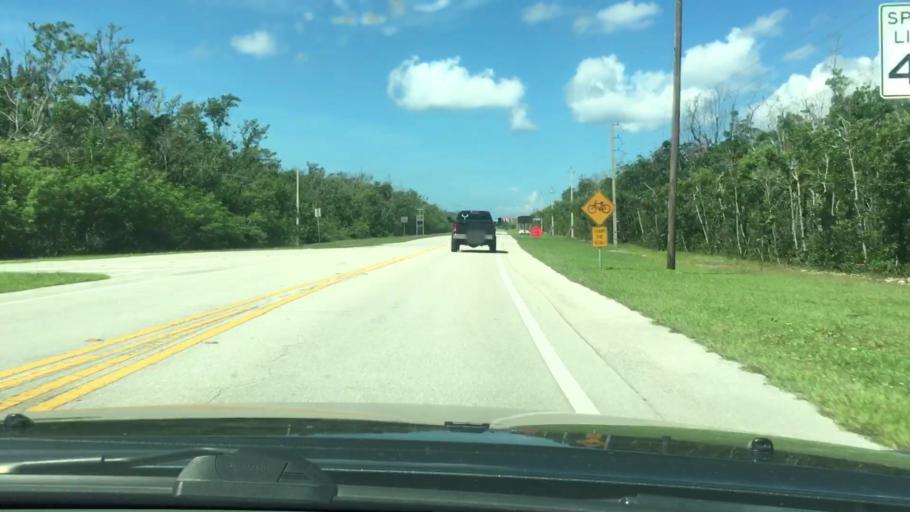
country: US
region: Florida
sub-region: Collier County
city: Marco
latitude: 25.9323
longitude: -81.6581
